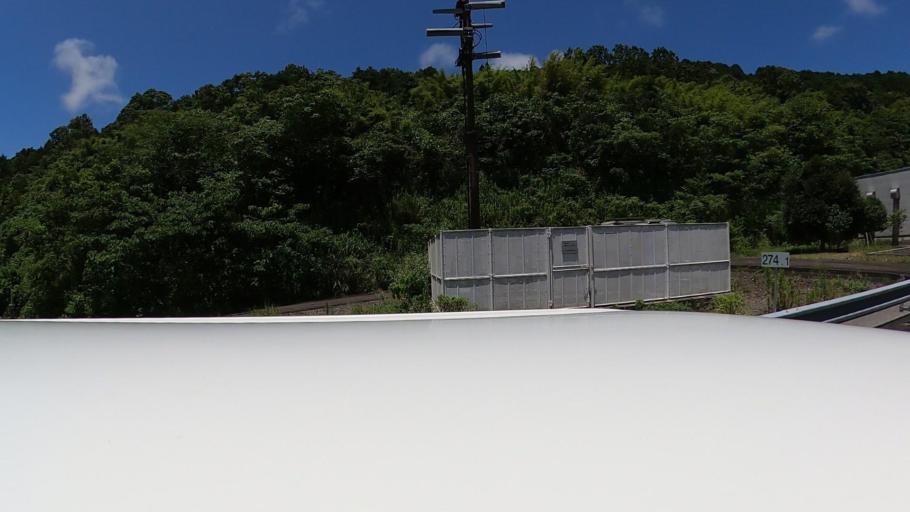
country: JP
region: Miyazaki
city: Nobeoka
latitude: 32.3522
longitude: 131.6083
